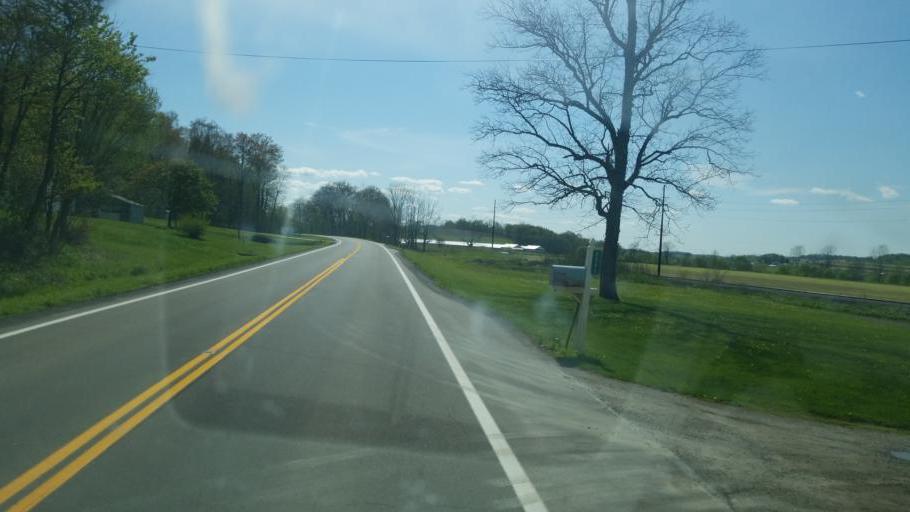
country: US
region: Ohio
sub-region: Tuscarawas County
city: Sugarcreek
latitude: 40.4671
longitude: -81.6820
